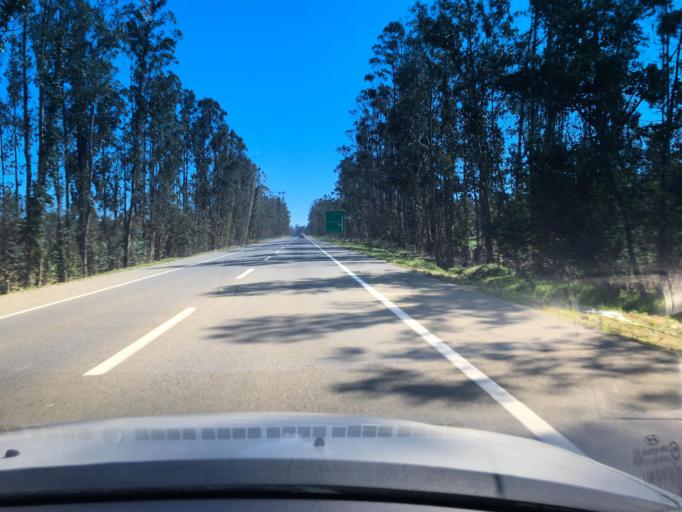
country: CL
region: Valparaiso
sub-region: San Antonio Province
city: El Tabo
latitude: -33.4020
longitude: -71.5788
